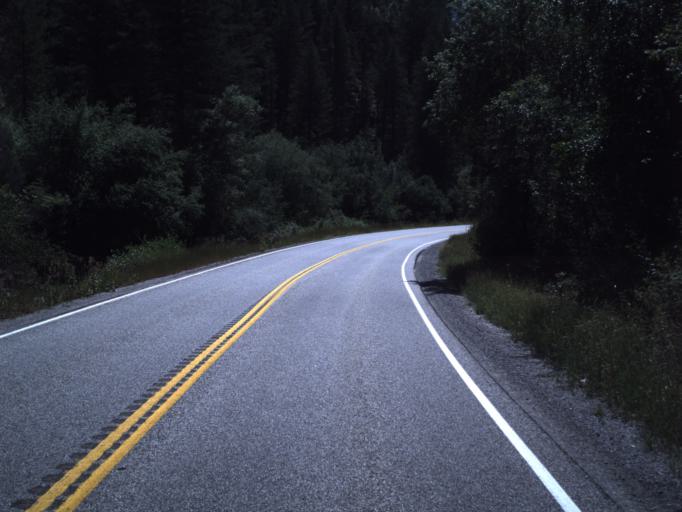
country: US
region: Utah
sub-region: Cache County
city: North Logan
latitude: 41.8121
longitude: -111.6249
